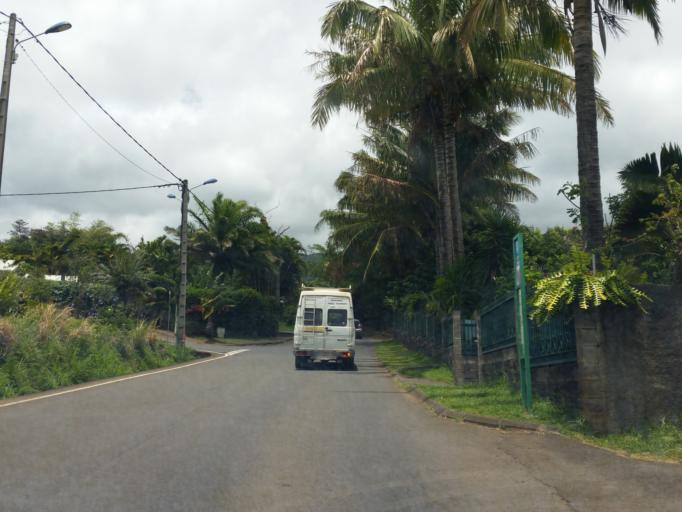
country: RE
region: Reunion
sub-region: Reunion
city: Sainte-Marie
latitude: -20.9301
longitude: 55.5416
